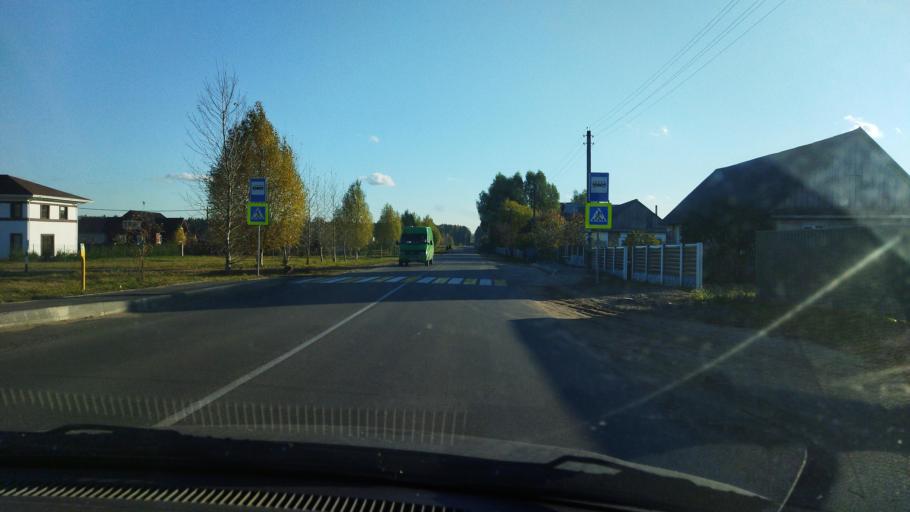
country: BY
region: Minsk
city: Korolev Stan
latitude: 53.9491
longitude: 27.8428
